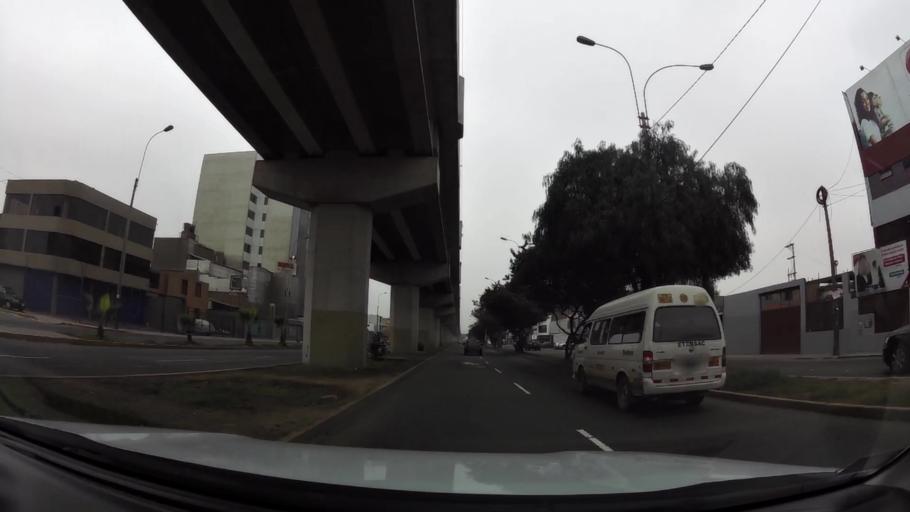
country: PE
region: Lima
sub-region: Lima
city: Surco
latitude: -12.1363
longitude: -76.9959
